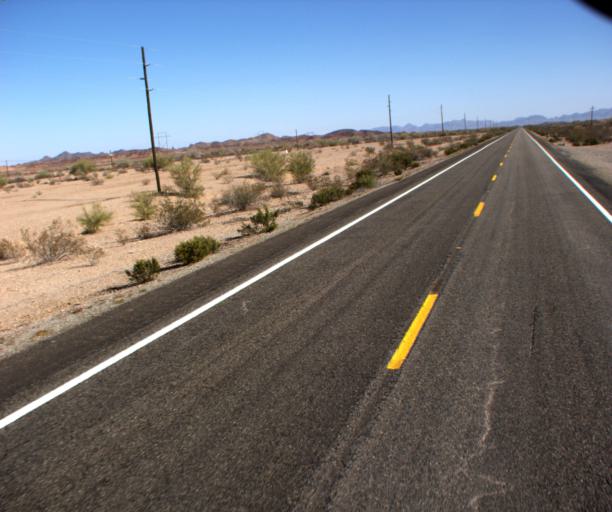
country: US
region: Arizona
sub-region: Yuma County
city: Fortuna Foothills
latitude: 32.9223
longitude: -114.3187
